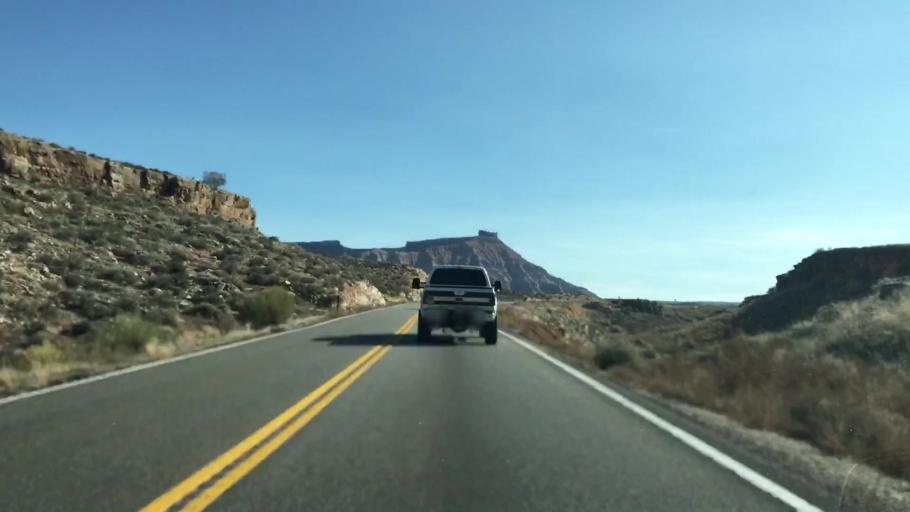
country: US
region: Utah
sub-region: Washington County
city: Hurricane
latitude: 37.1691
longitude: -113.2661
